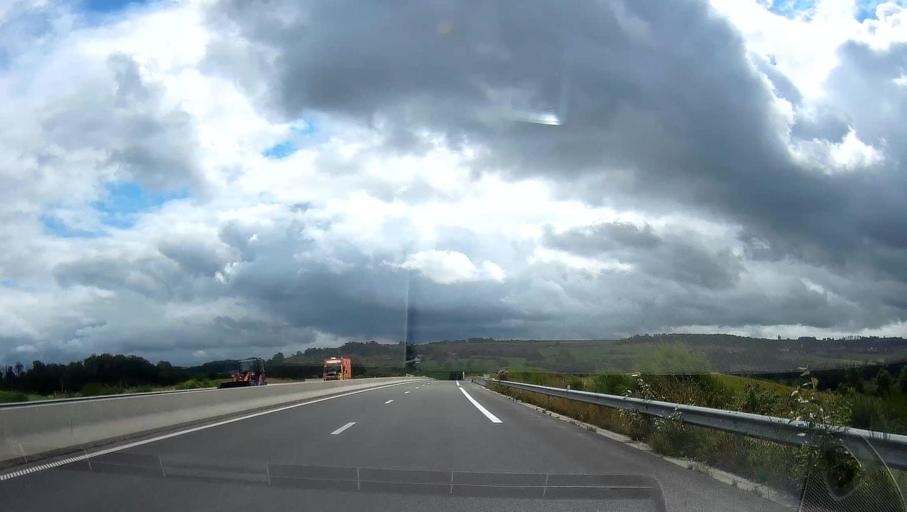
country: FR
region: Champagne-Ardenne
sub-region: Departement des Ardennes
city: Rimogne
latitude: 49.8007
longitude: 4.5328
